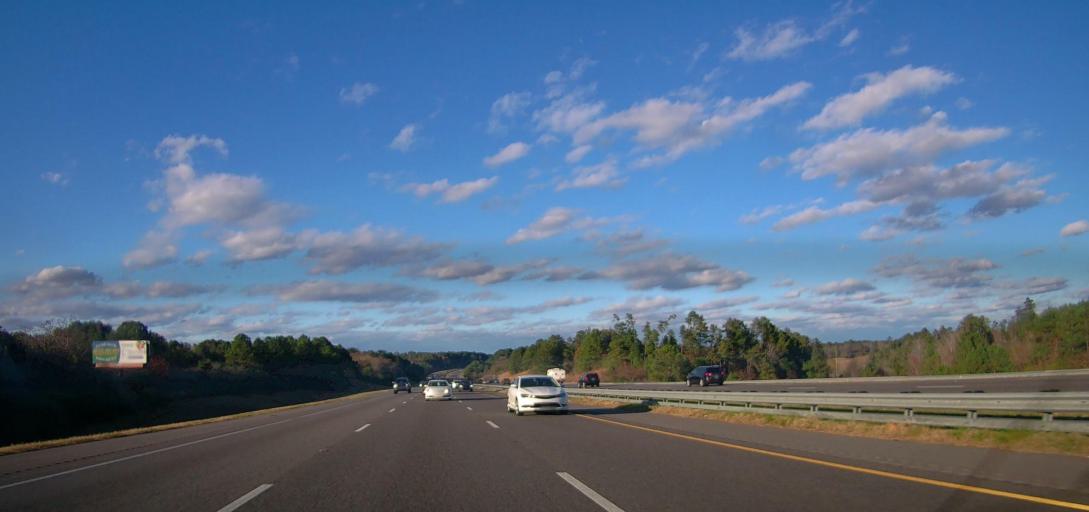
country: US
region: Alabama
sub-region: Jefferson County
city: Morris
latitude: 33.7525
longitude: -86.8290
